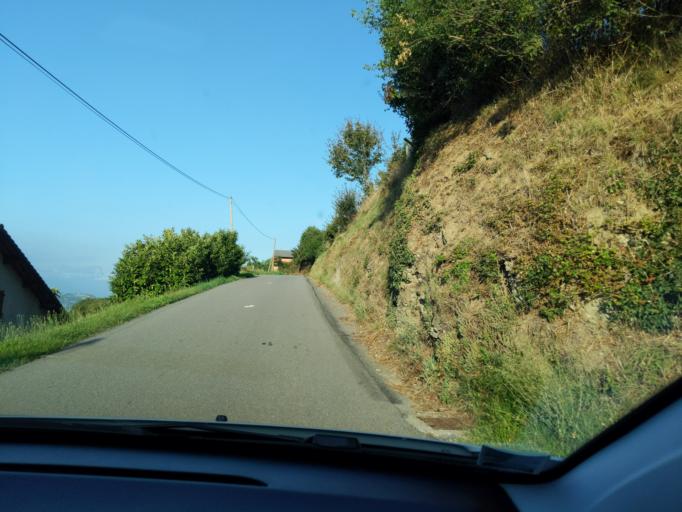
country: FR
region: Rhone-Alpes
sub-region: Departement de la Savoie
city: Aiton
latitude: 45.5616
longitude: 6.2660
